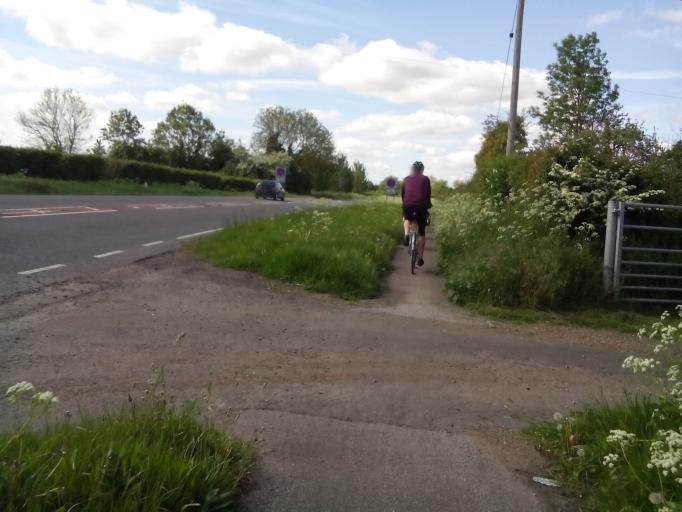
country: GB
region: England
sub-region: Cambridgeshire
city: Harston
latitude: 52.1337
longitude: 0.0734
